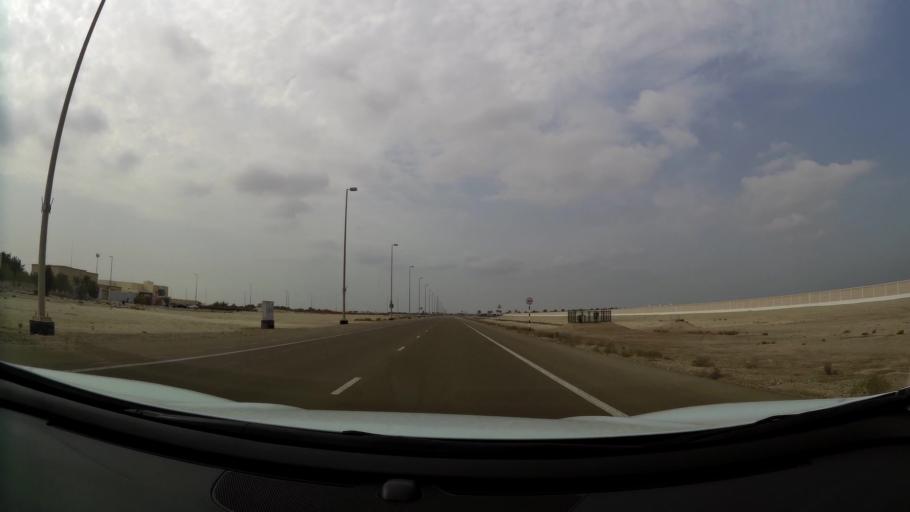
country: AE
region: Abu Dhabi
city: Abu Dhabi
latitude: 24.6327
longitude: 54.6565
